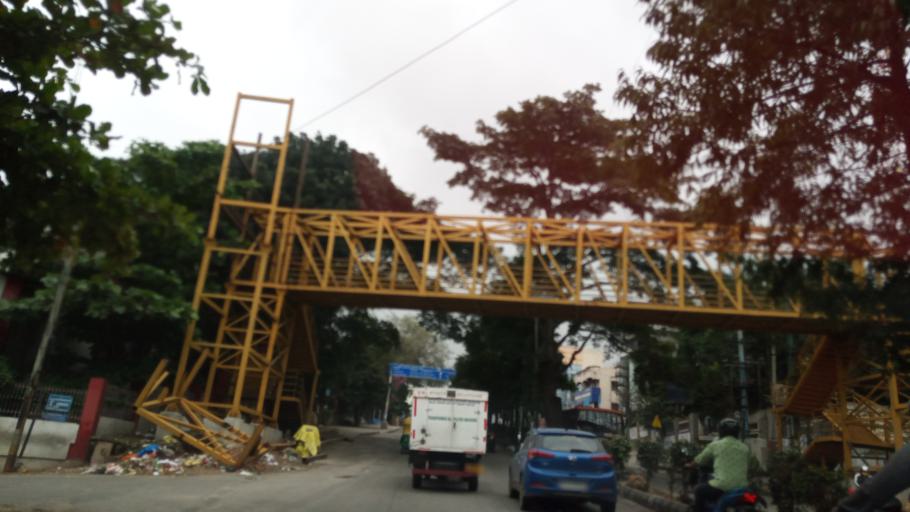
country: IN
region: Karnataka
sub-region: Bangalore Urban
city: Bangalore
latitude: 12.9322
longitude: 77.5415
